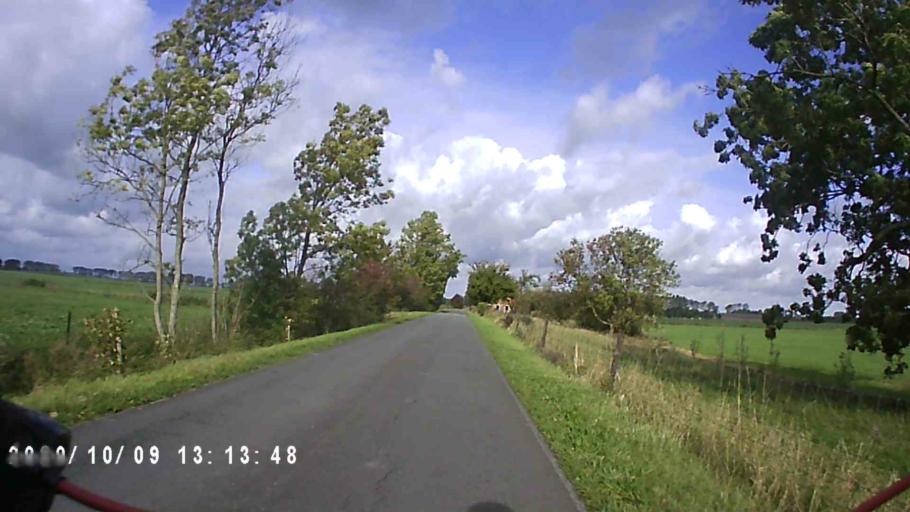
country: NL
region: Groningen
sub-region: Gemeente Zuidhorn
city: Aduard
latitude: 53.2482
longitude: 6.4360
